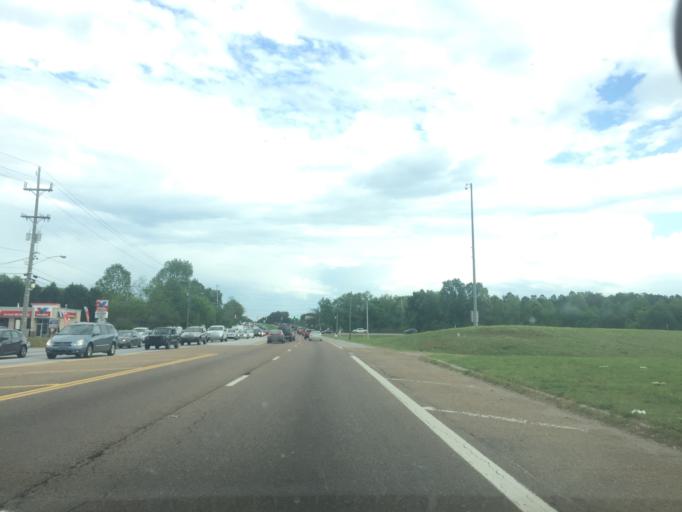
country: US
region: Tennessee
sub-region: Hamilton County
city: Red Bank
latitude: 35.1216
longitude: -85.2384
